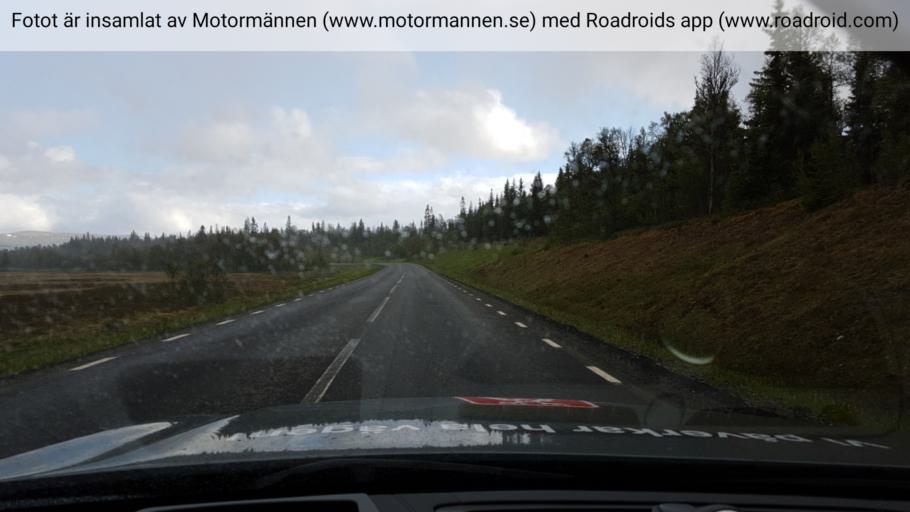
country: NO
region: Nord-Trondelag
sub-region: Meraker
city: Meraker
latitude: 63.5670
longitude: 12.2874
